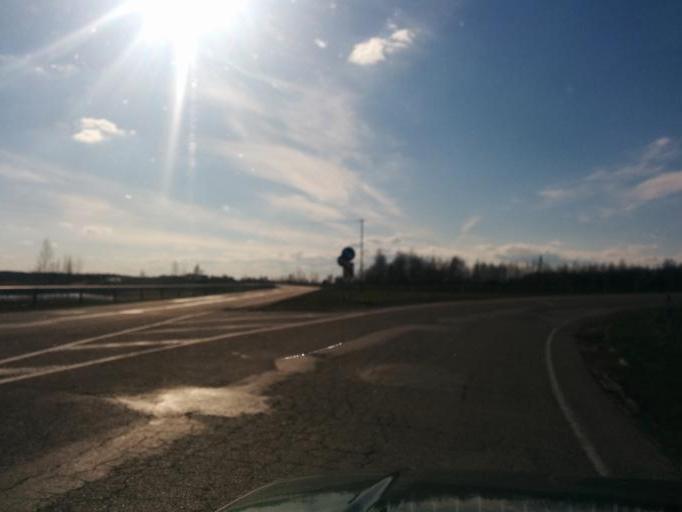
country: LV
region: Ozolnieku
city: Ozolnieki
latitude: 56.6487
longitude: 23.7997
